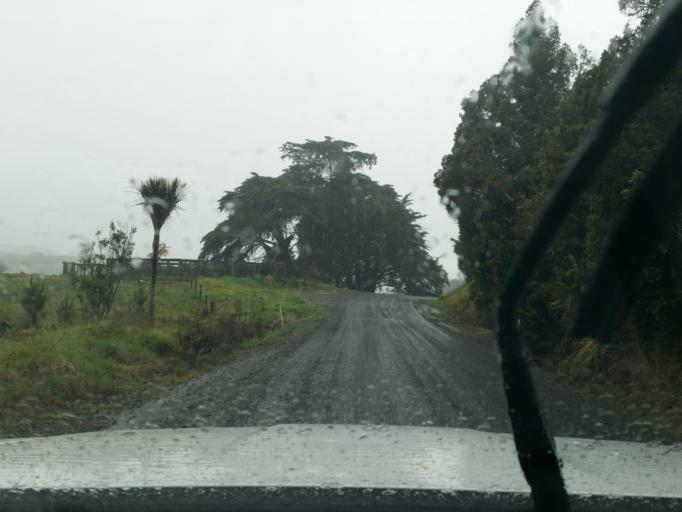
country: NZ
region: Northland
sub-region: Kaipara District
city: Dargaville
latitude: -35.7516
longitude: 173.9594
